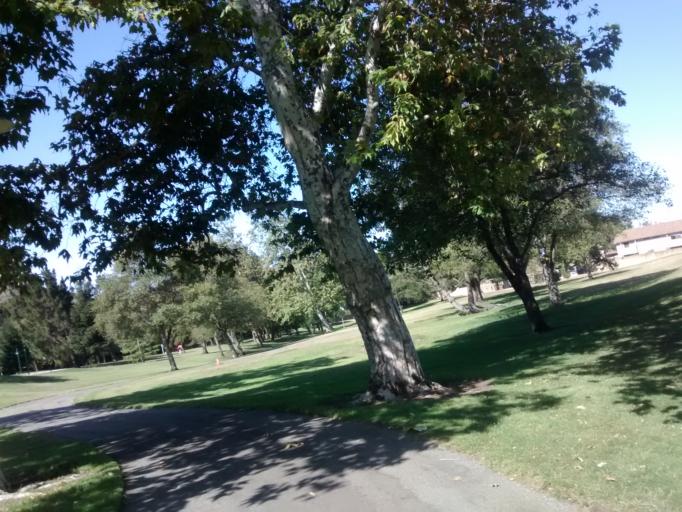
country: US
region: California
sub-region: San Luis Obispo County
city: San Luis Obispo
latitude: 35.2687
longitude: -120.6589
